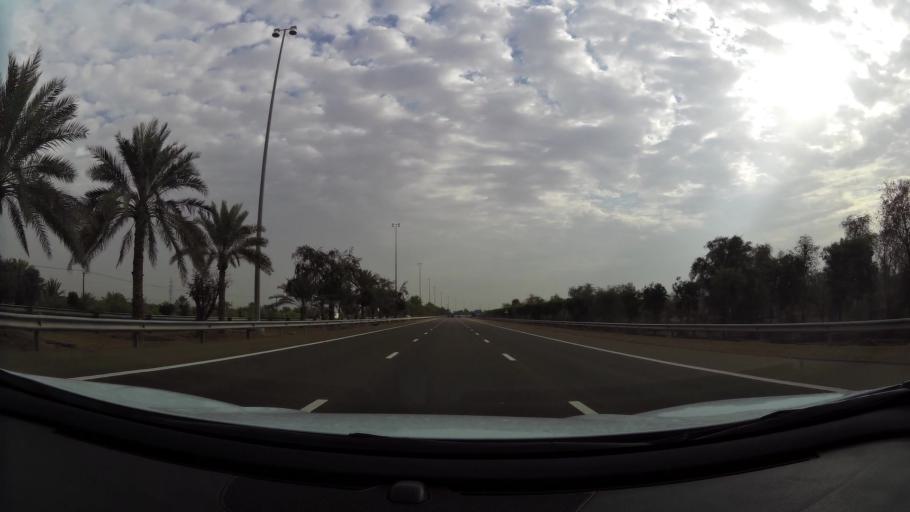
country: AE
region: Abu Dhabi
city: Al Ain
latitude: 24.1976
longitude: 55.3644
